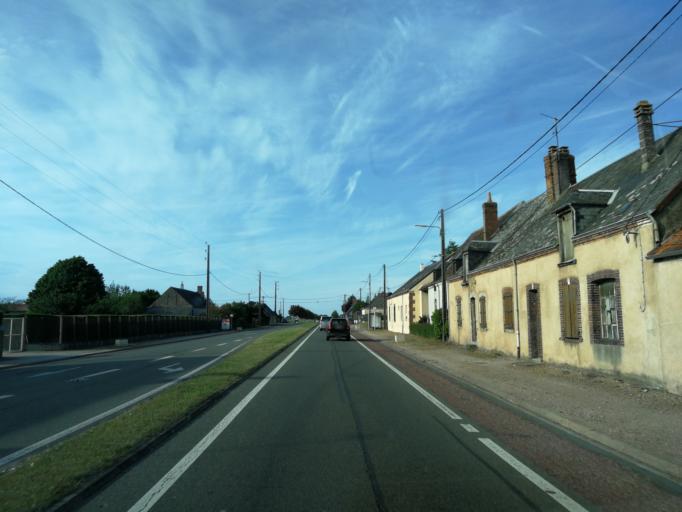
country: FR
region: Centre
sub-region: Departement d'Eure-et-Loir
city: Marboue
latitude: 48.1471
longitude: 1.3508
